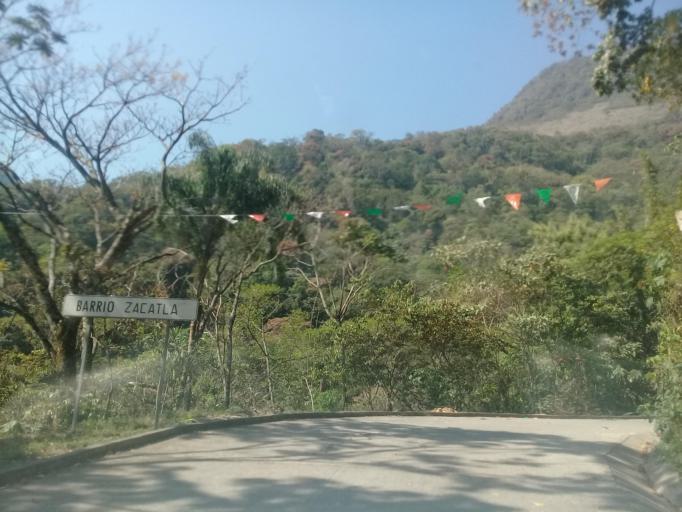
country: MX
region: Veracruz
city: Rafael Delgado
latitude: 18.7821
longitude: -97.0265
